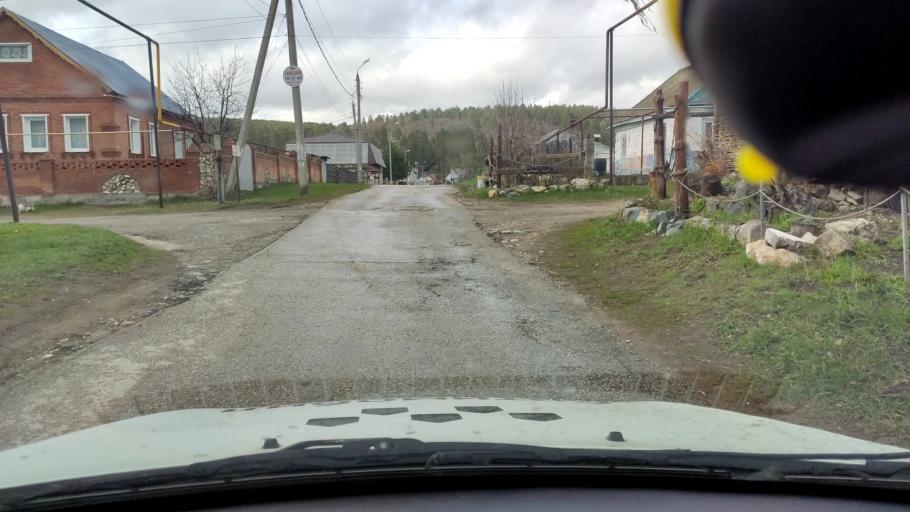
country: RU
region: Samara
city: Zhigulevsk
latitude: 53.4675
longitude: 49.6033
